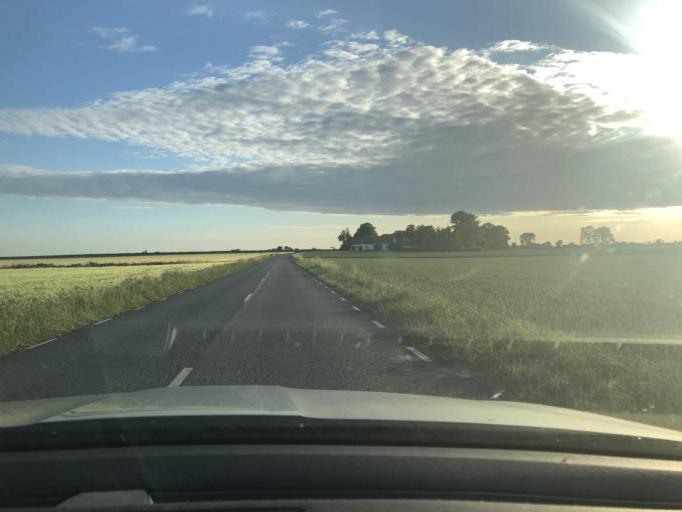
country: SE
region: Skane
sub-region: Ystads Kommun
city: Kopingebro
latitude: 55.4283
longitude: 14.1598
